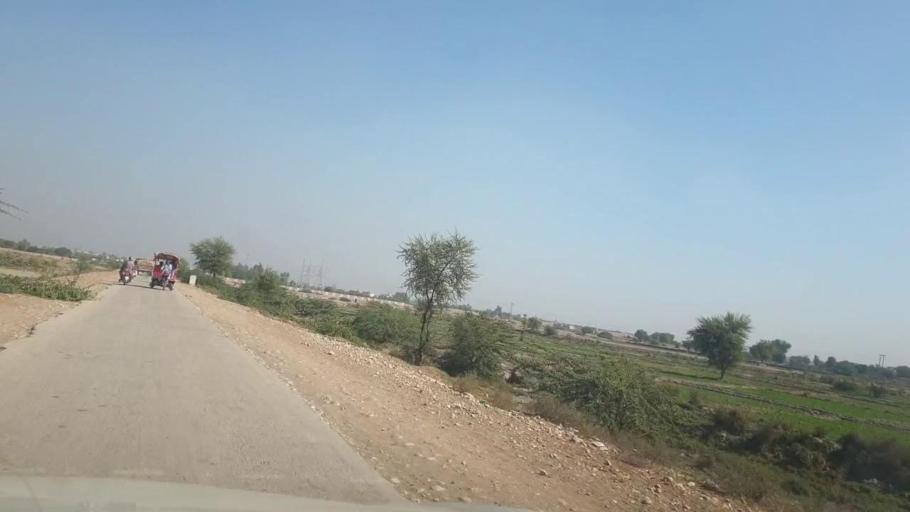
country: PK
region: Sindh
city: Bhan
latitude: 26.5448
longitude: 67.7076
